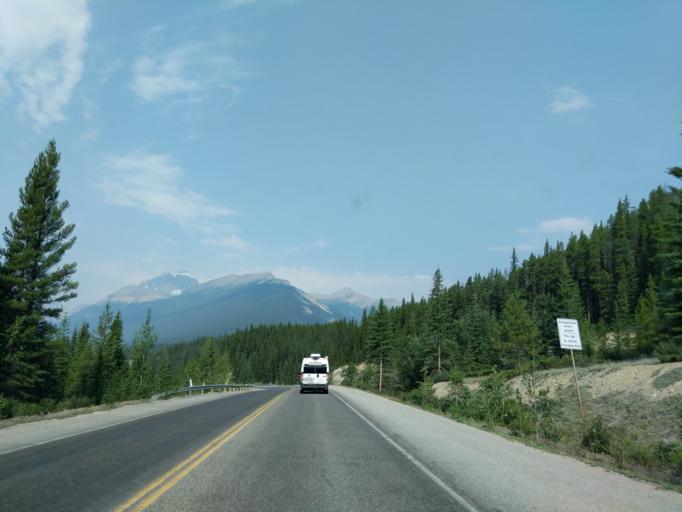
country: CA
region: British Columbia
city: Golden
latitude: 52.0675
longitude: -116.9009
